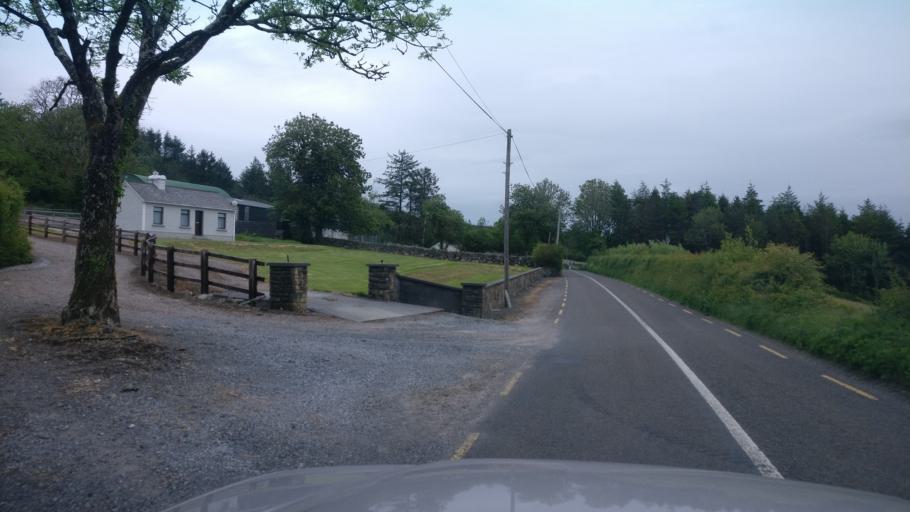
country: IE
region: Connaught
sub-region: County Galway
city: Loughrea
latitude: 53.0677
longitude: -8.6011
